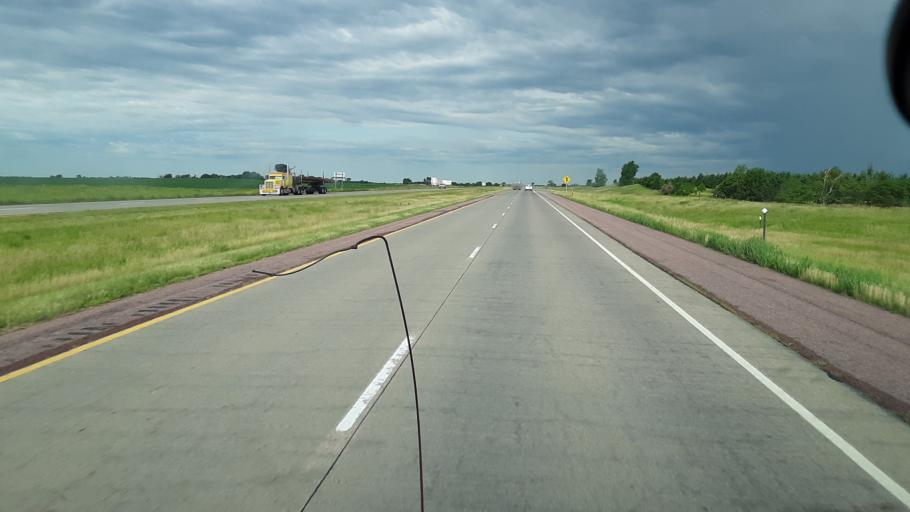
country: US
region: South Dakota
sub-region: Hanson County
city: Alexandria
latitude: 43.6653
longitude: -97.5908
